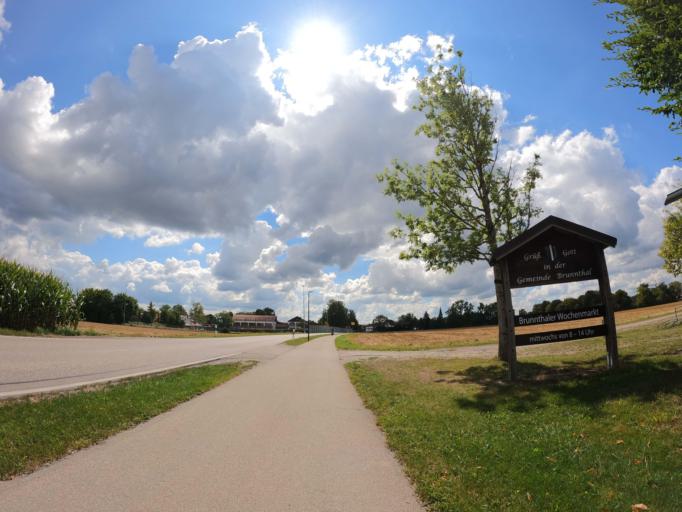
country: DE
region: Bavaria
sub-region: Upper Bavaria
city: Brunnthal
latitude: 48.0102
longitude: 11.6848
